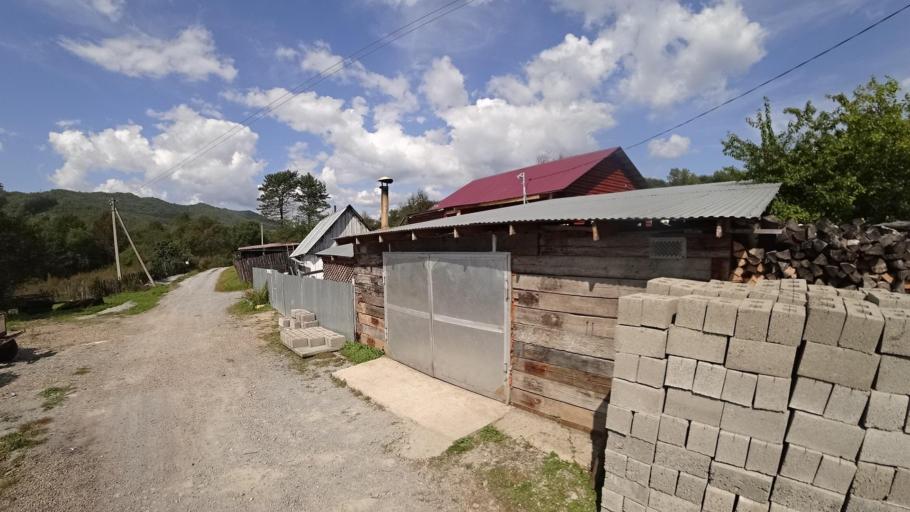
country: RU
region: Jewish Autonomous Oblast
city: Londoko
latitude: 49.0284
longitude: 131.9299
